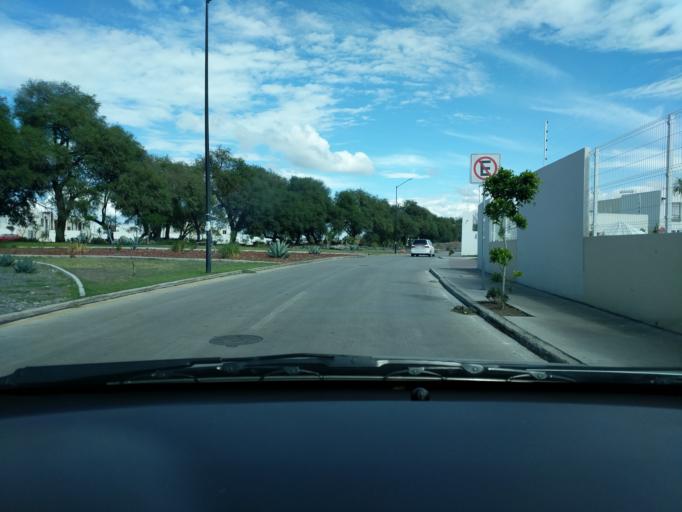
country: MX
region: Queretaro
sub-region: El Marques
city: La Loma
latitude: 20.5846
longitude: -100.2551
